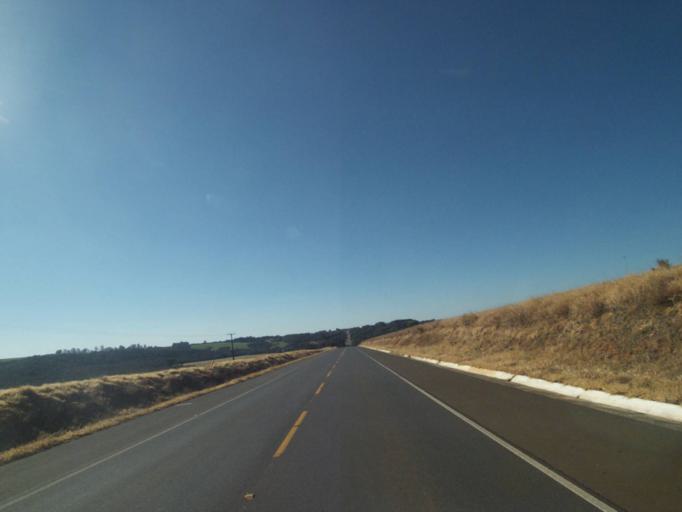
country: BR
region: Parana
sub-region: Tibagi
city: Tibagi
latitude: -24.6205
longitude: -50.4499
